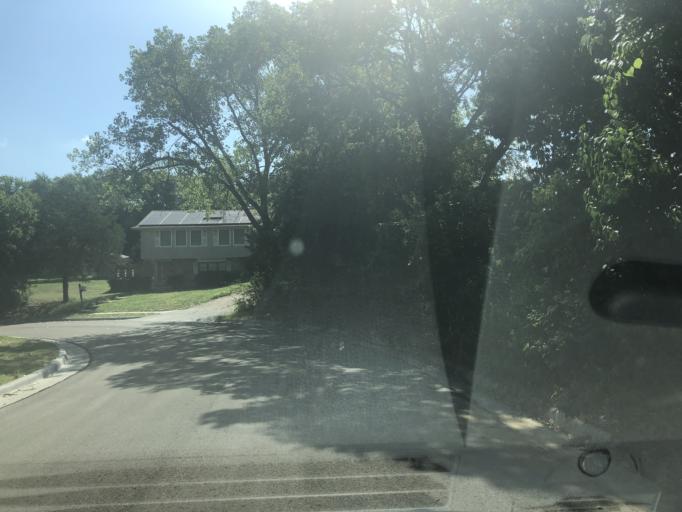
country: US
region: Texas
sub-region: Dallas County
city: Grand Prairie
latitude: 32.7569
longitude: -97.0002
